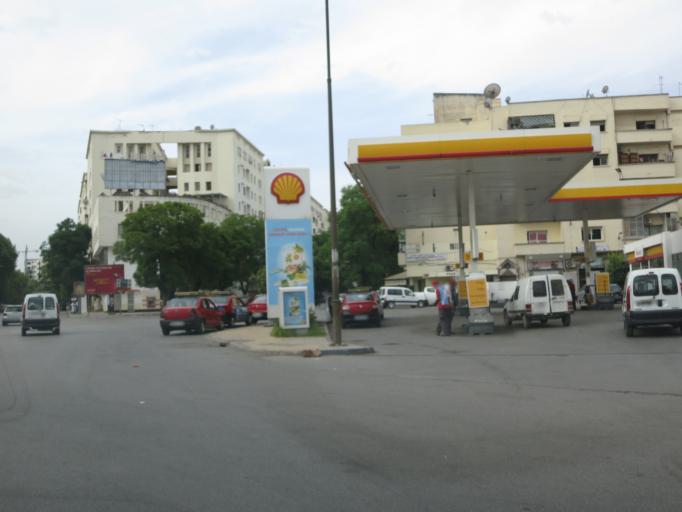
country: MA
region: Fes-Boulemane
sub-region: Fes
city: Fes
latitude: 34.0433
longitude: -5.0035
